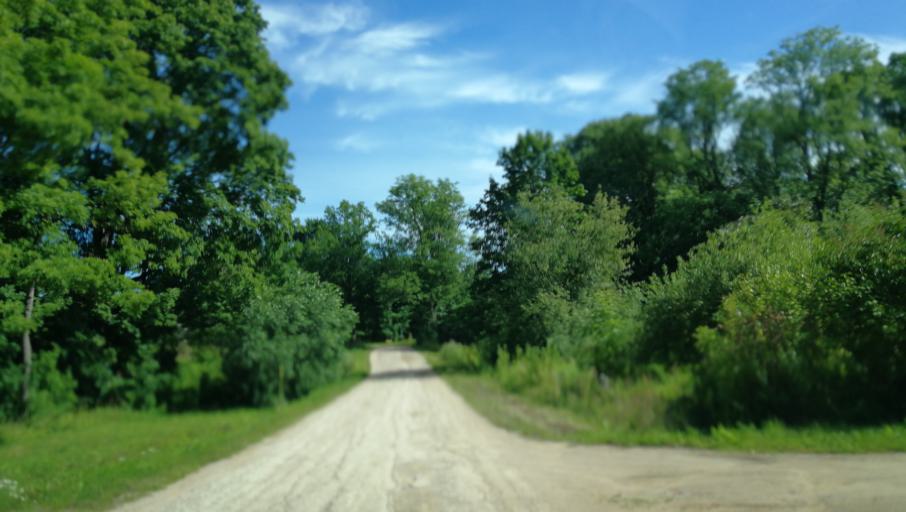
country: LV
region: Gulbenes Rajons
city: Gulbene
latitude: 57.1750
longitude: 26.8731
